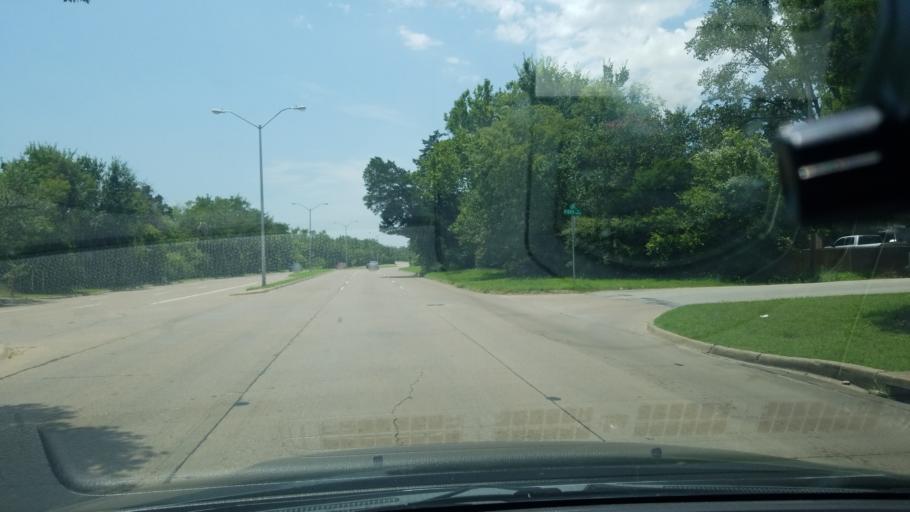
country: US
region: Texas
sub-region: Dallas County
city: Balch Springs
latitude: 32.7285
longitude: -96.6657
